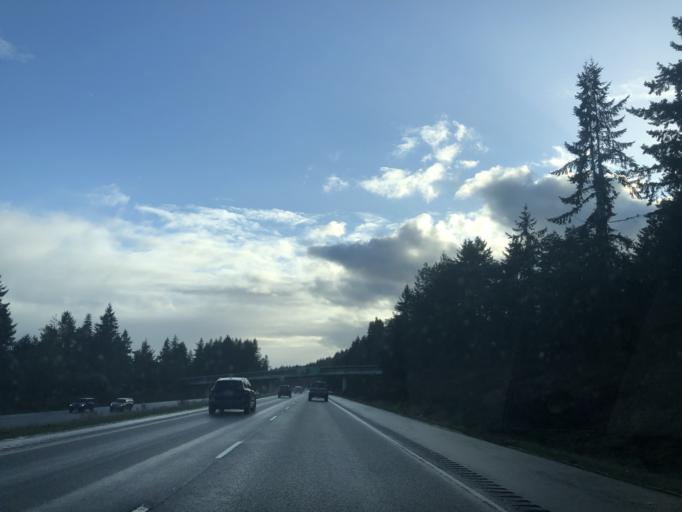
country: US
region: Washington
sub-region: Kitsap County
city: Chico
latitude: 47.6180
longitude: -122.7120
